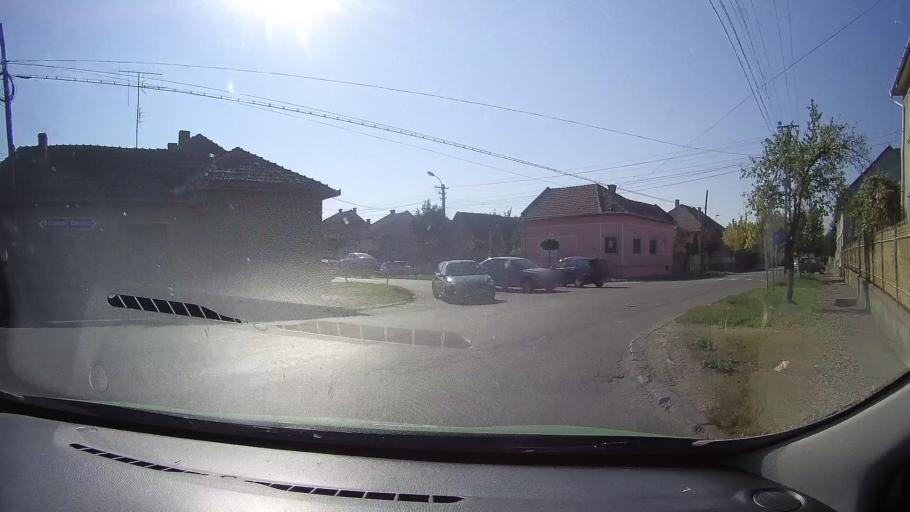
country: RO
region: Satu Mare
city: Carei
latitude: 47.6931
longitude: 22.4730
